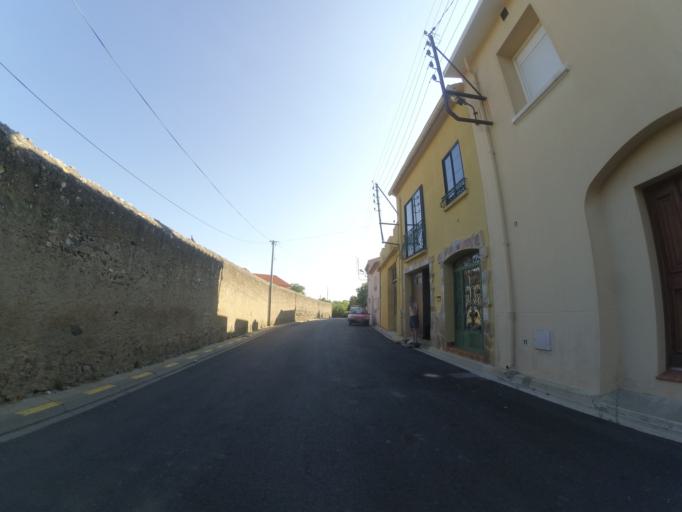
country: FR
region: Languedoc-Roussillon
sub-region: Departement des Pyrenees-Orientales
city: Peyrestortes
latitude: 42.7797
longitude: 2.8377
